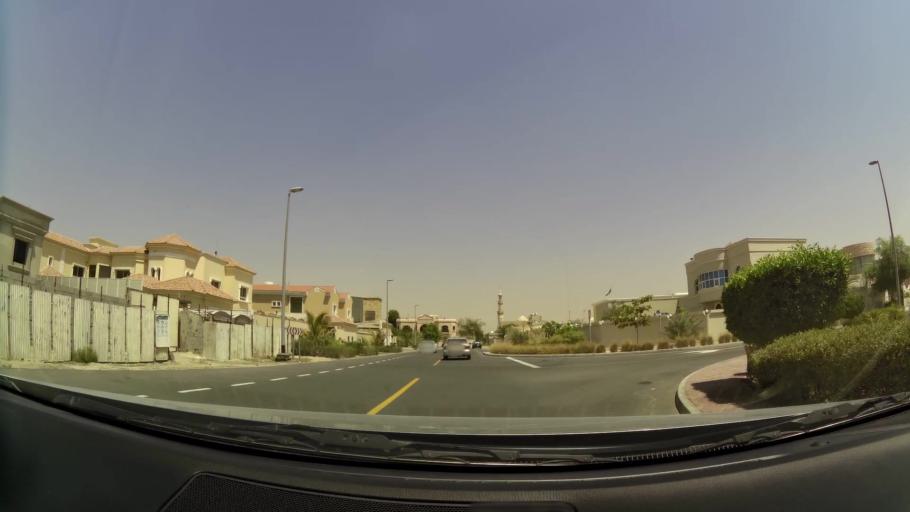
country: AE
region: Dubai
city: Dubai
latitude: 25.1072
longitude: 55.2215
